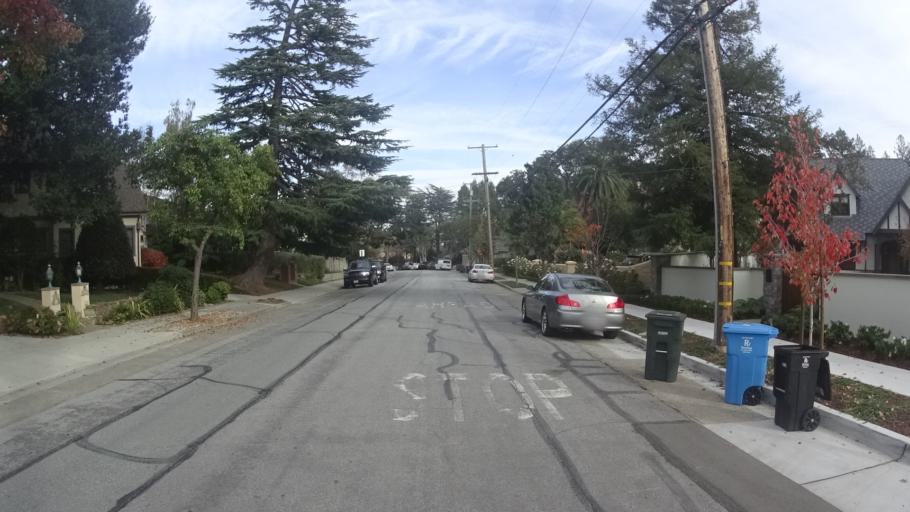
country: US
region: California
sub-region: San Mateo County
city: Hillsborough
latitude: 37.5802
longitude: -122.3748
